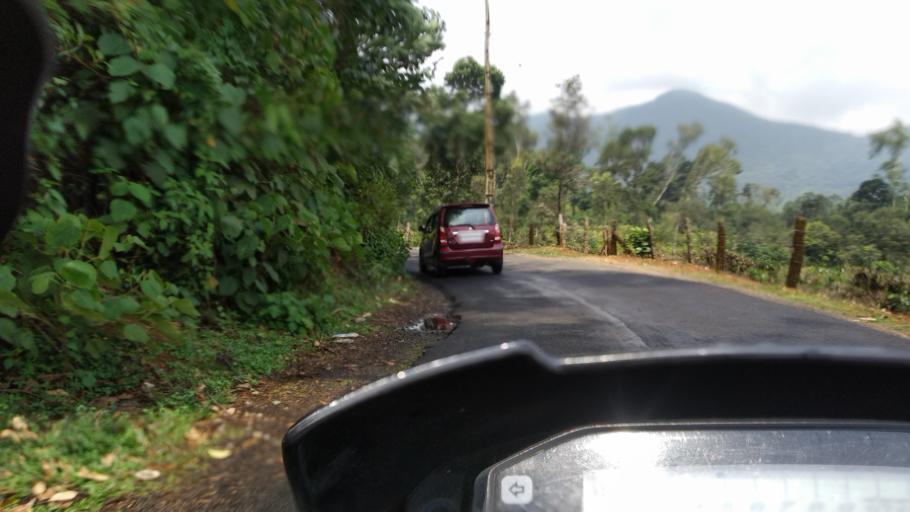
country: IN
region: Kerala
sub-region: Kottayam
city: Erattupetta
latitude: 9.6302
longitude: 76.9637
